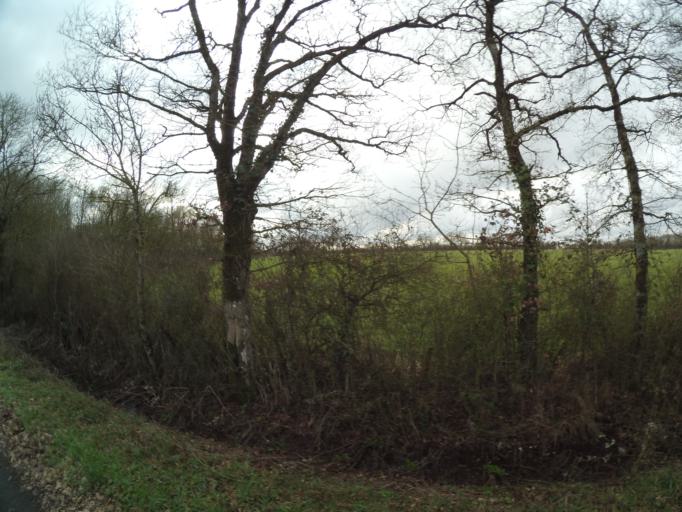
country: FR
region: Pays de la Loire
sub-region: Departement de la Vendee
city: La Bernardiere
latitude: 47.0294
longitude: -1.2934
